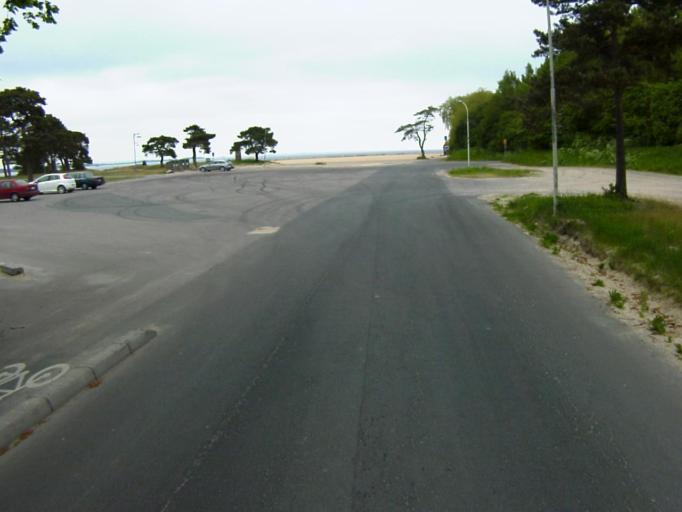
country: SE
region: Skane
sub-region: Kristianstads Kommun
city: Ahus
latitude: 55.9314
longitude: 14.3188
